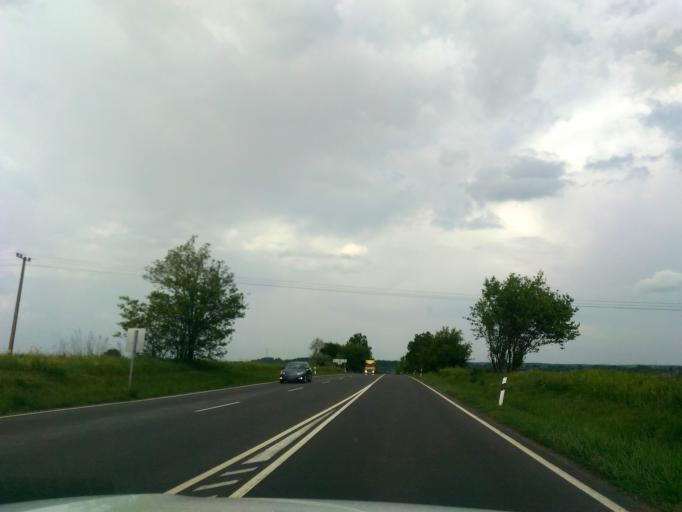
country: HU
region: Tolna
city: Bonyhad
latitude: 46.2798
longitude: 18.5207
